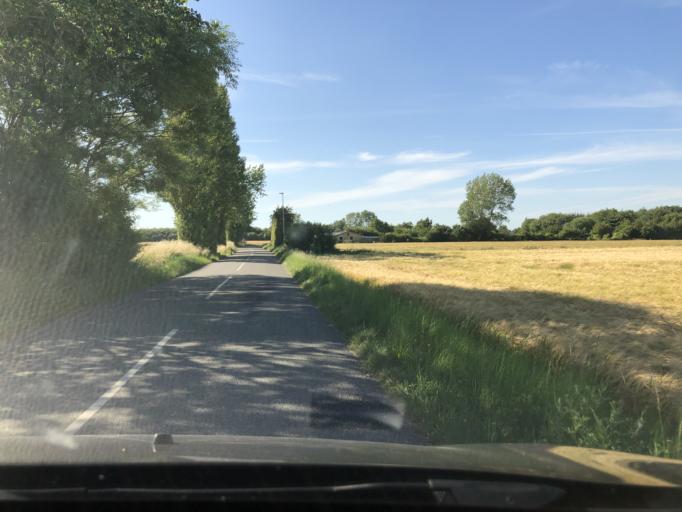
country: DK
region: South Denmark
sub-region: AEro Kommune
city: Marstal
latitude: 54.8633
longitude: 10.5055
